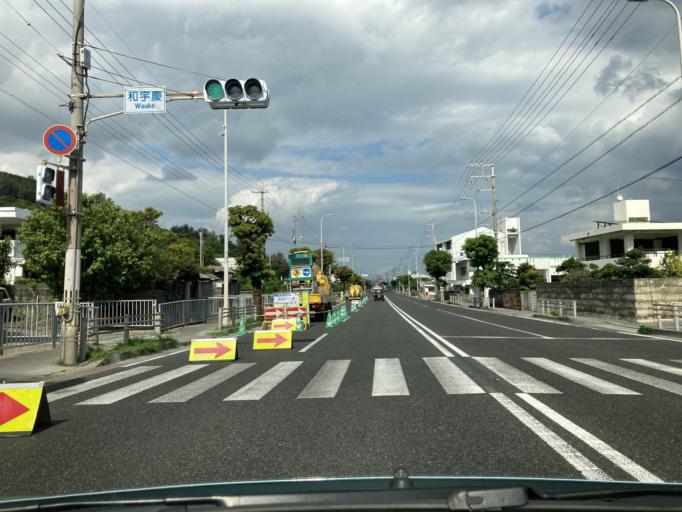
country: JP
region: Okinawa
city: Ginowan
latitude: 26.2418
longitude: 127.7789
